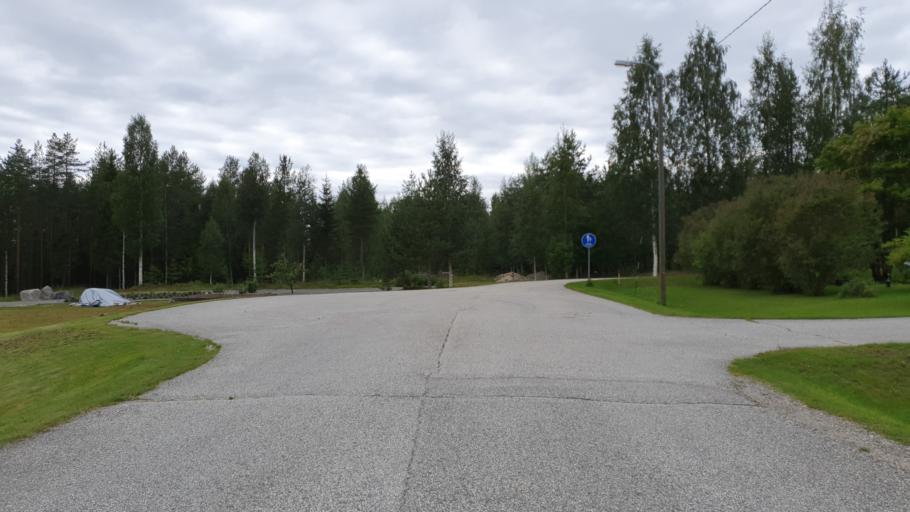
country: FI
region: Kainuu
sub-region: Kehys-Kainuu
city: Kuhmo
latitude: 64.1366
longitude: 29.4537
